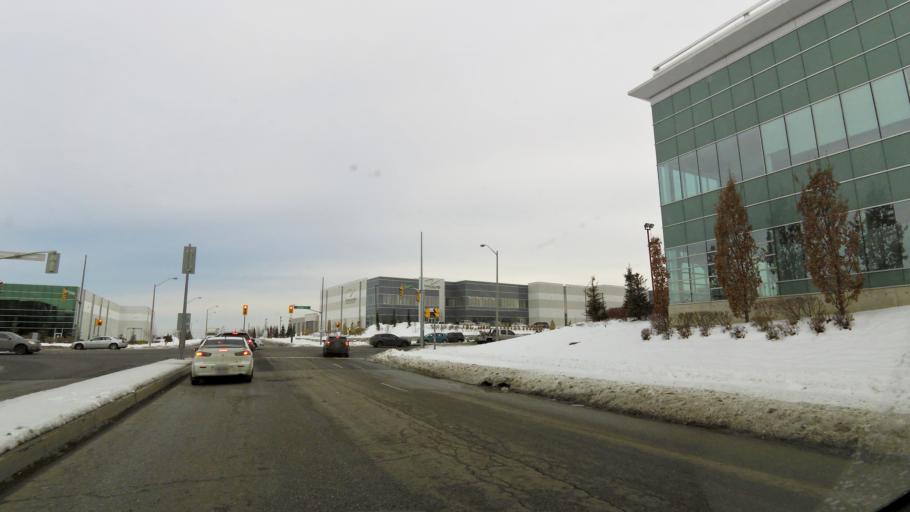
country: CA
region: Ontario
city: Etobicoke
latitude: 43.7756
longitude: -79.6440
